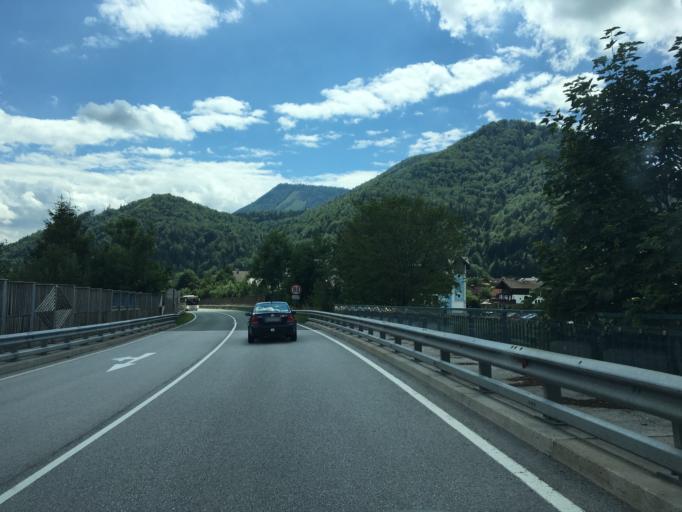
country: AT
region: Salzburg
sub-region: Politischer Bezirk Salzburg-Umgebung
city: Ebenau
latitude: 47.7937
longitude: 13.1740
